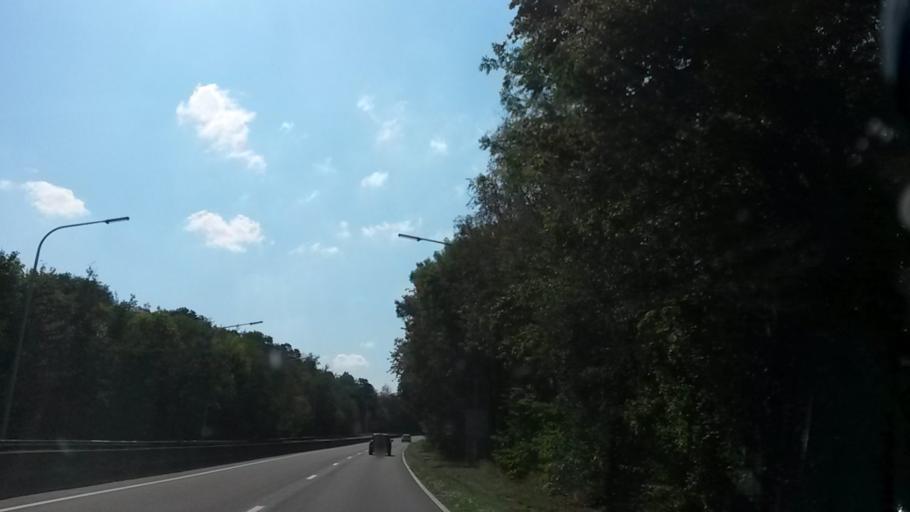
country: BE
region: Wallonia
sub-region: Province de Namur
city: Fosses-la-Ville
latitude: 50.4432
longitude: 4.7035
